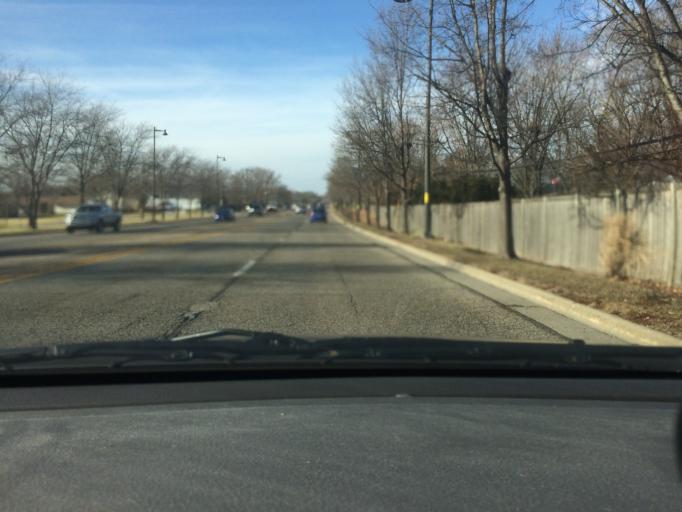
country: US
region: Illinois
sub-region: Cook County
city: Streamwood
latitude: 42.0098
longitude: -88.1642
